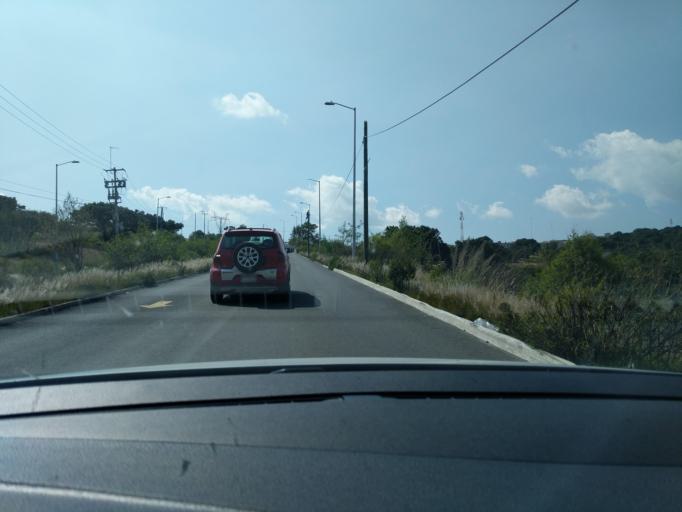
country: MX
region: Puebla
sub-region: Puebla
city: Galaxia la Calera
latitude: 19.0160
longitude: -98.1387
